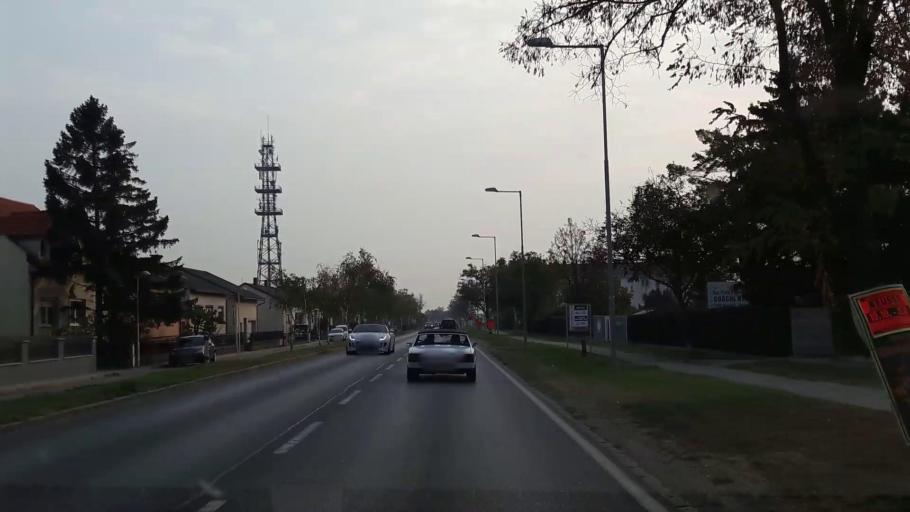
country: AT
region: Burgenland
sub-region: Politischer Bezirk Neusiedl am See
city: Neusiedl am See
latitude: 47.9647
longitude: 16.8375
